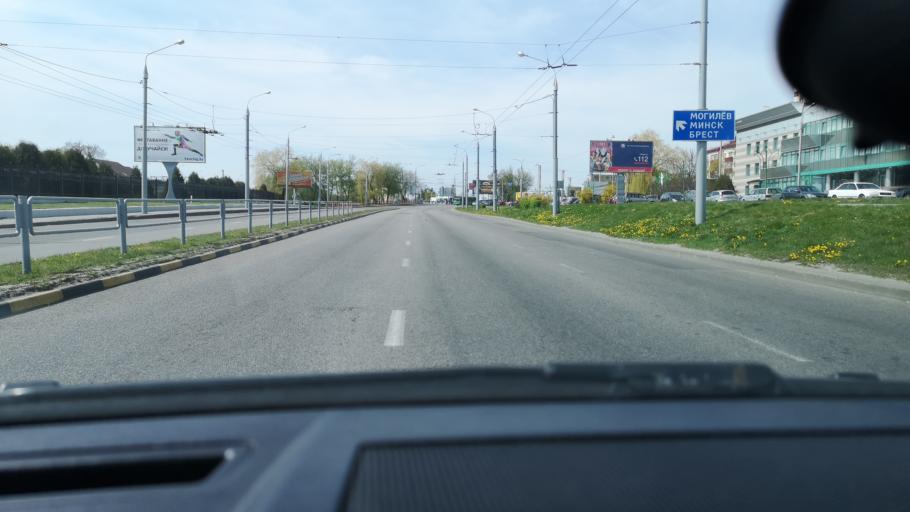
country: BY
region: Gomel
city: Gomel
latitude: 52.4149
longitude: 31.0030
